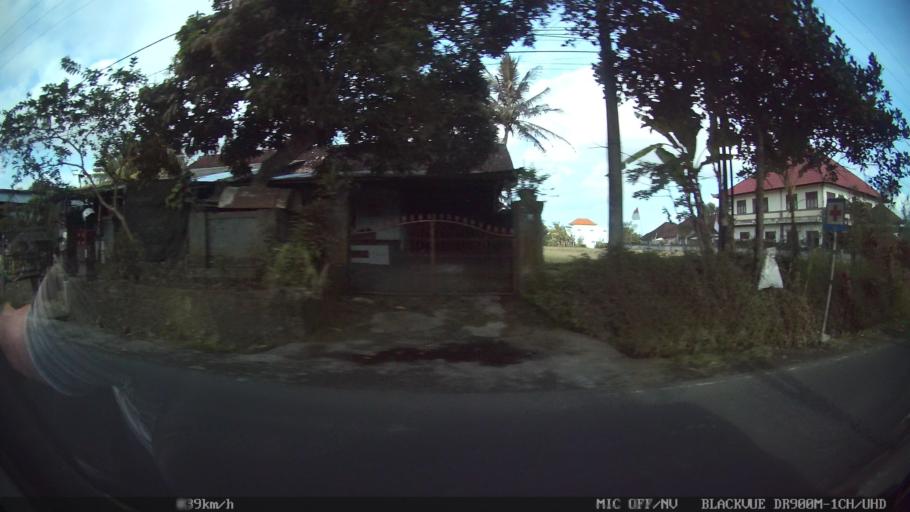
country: ID
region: Bali
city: Banjar Sedang
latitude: -8.5634
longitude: 115.2342
